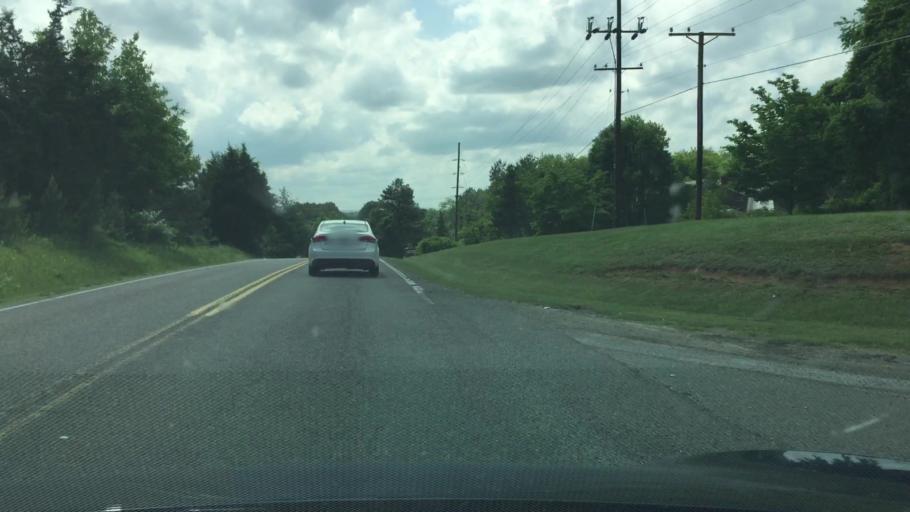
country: US
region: Virginia
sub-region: Pulaski County
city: Dublin
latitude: 37.0802
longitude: -80.6754
